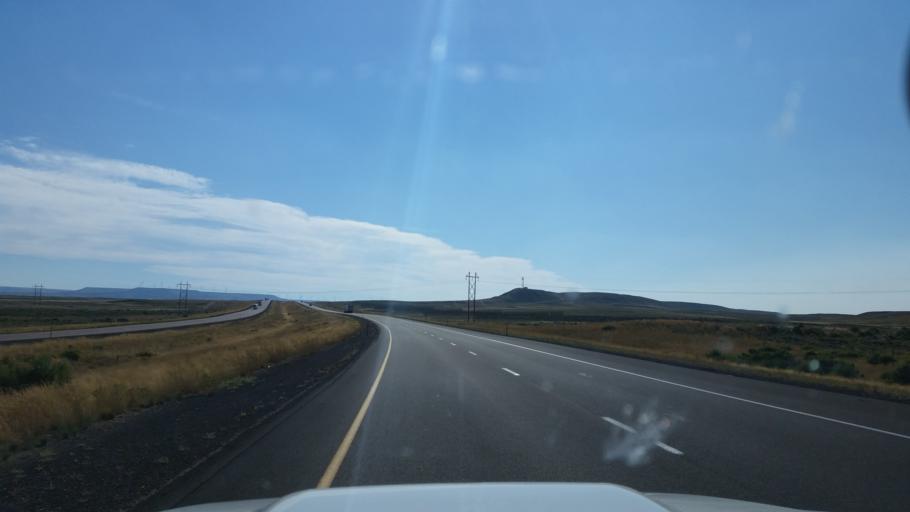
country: US
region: Wyoming
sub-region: Uinta County
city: Lyman
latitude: 41.3539
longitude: -110.3719
